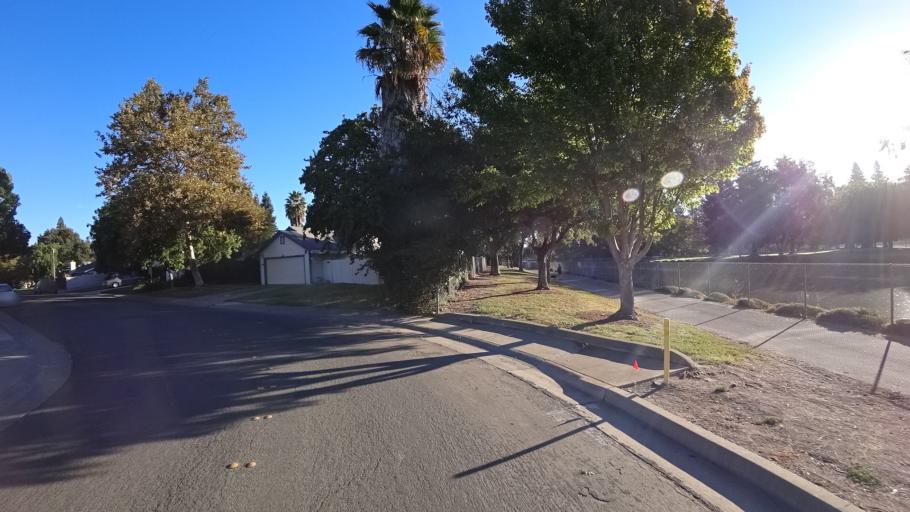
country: US
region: California
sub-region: Sacramento County
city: Parkway
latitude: 38.4848
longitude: -121.5434
